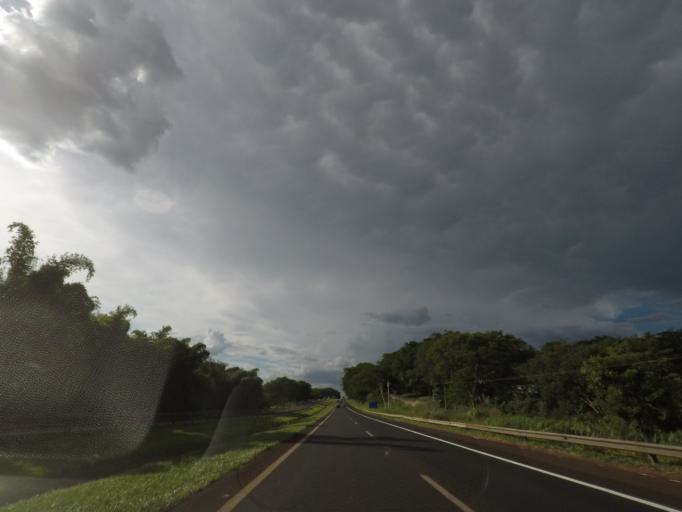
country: BR
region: Sao Paulo
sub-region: Jardinopolis
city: Jardinopolis
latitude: -21.0651
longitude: -47.8158
